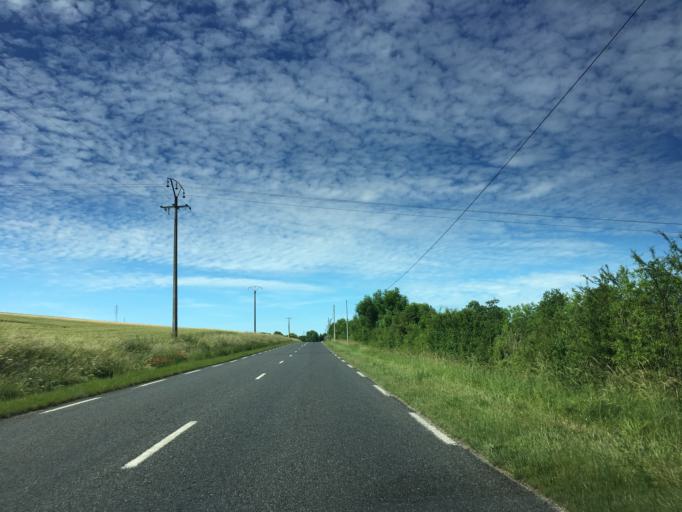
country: FR
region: Bourgogne
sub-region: Departement de l'Yonne
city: Auxerre
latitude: 47.7705
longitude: 3.5539
